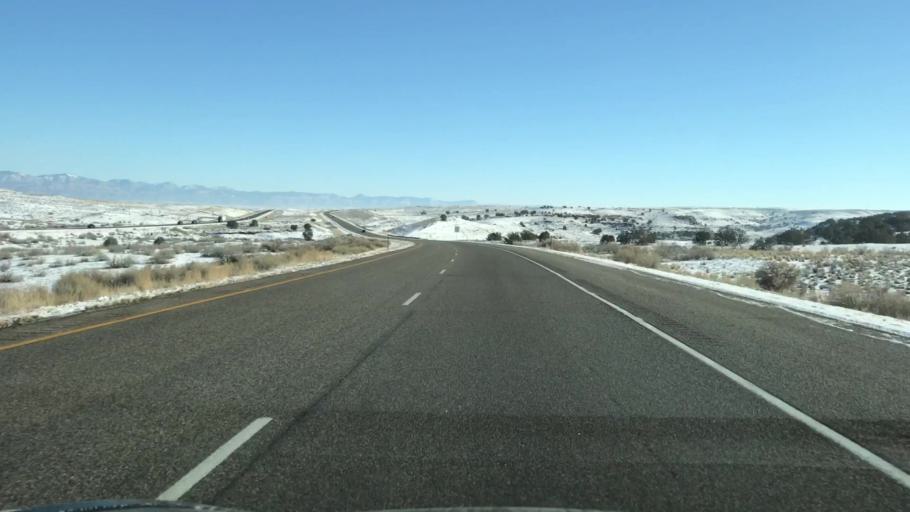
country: US
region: Colorado
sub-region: Mesa County
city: Loma
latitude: 39.2213
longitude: -108.9485
